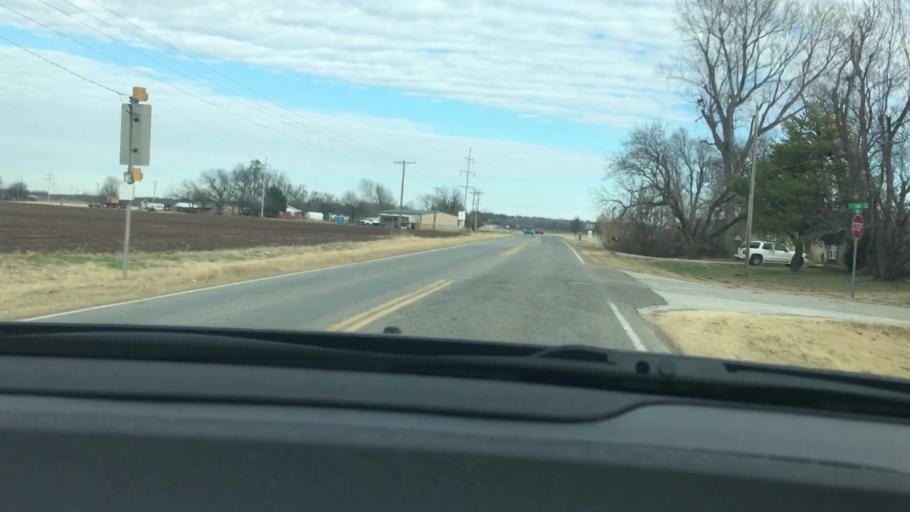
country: US
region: Oklahoma
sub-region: Garvin County
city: Pauls Valley
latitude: 34.7477
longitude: -97.2121
